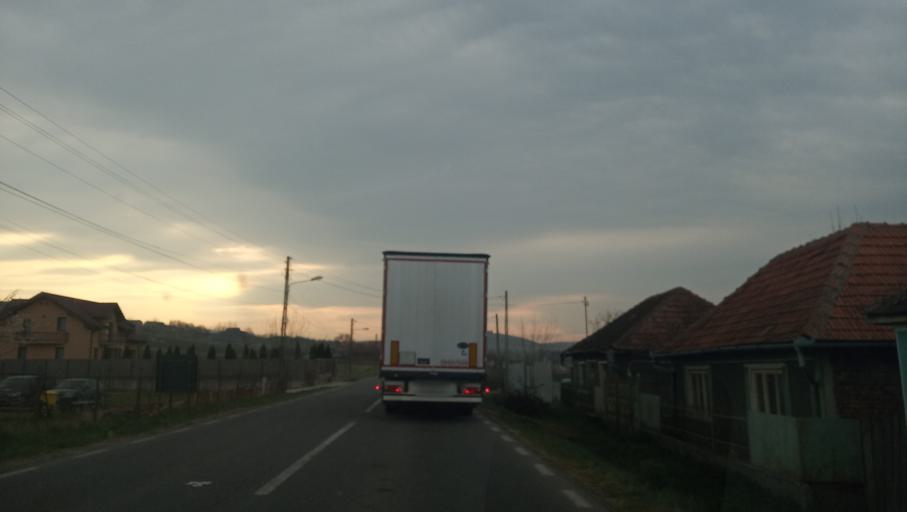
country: RO
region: Bihor
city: Hidiselu de Sus
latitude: 46.9457
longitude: 22.0246
